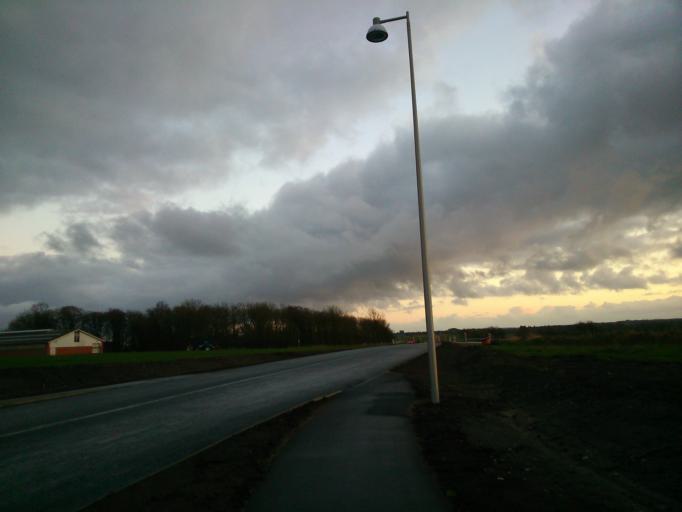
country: DK
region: Central Jutland
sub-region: Herning Kommune
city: Avlum
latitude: 56.2537
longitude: 8.7811
